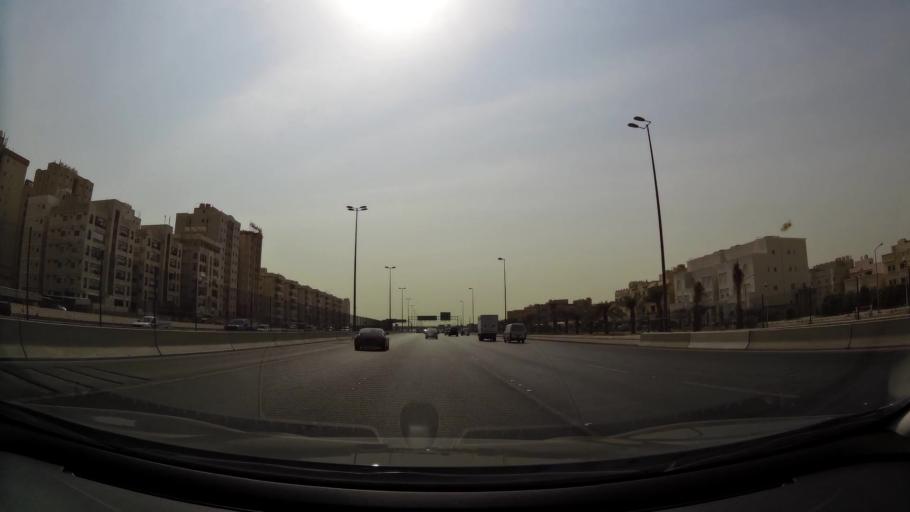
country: KW
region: Al Farwaniyah
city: Al Farwaniyah
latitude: 29.2730
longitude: 47.9508
